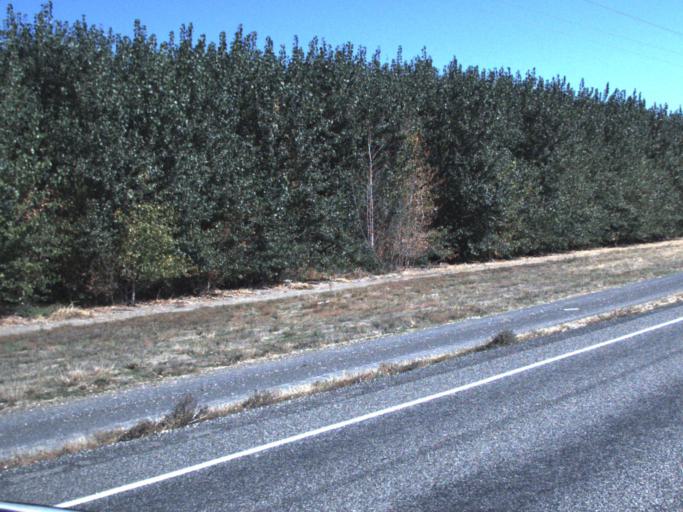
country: US
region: Washington
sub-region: Walla Walla County
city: Burbank
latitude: 46.2151
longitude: -118.8822
